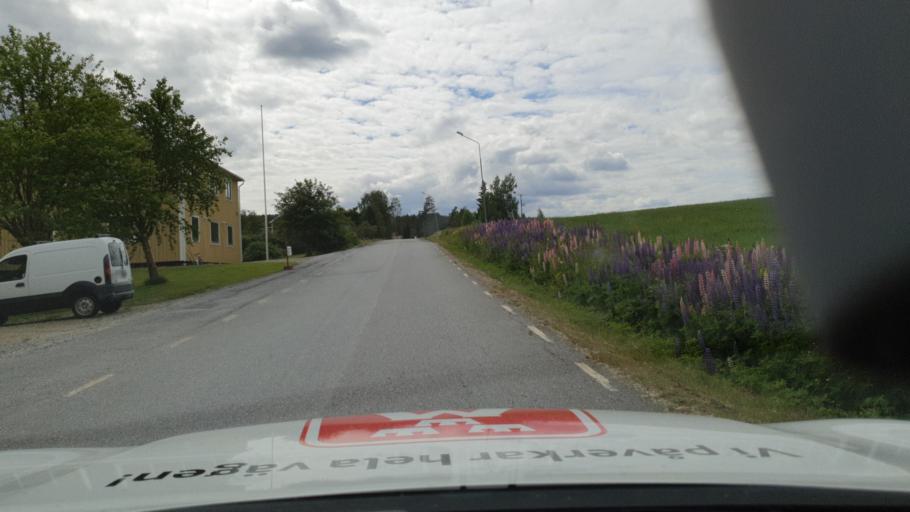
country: SE
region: Vaesterbotten
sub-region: Bjurholms Kommun
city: Bjurholm
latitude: 63.9147
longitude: 19.0865
